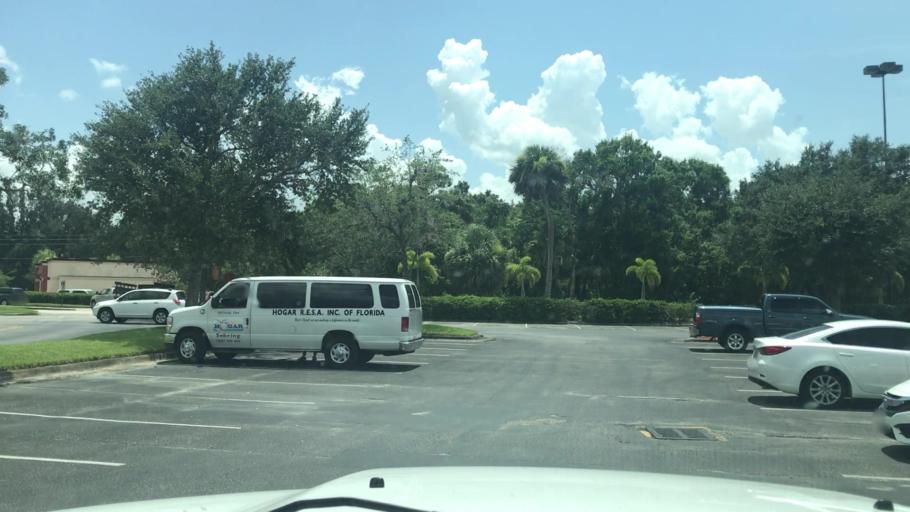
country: US
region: Florida
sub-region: Indian River County
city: West Vero Corridor
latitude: 27.6408
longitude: -80.4545
